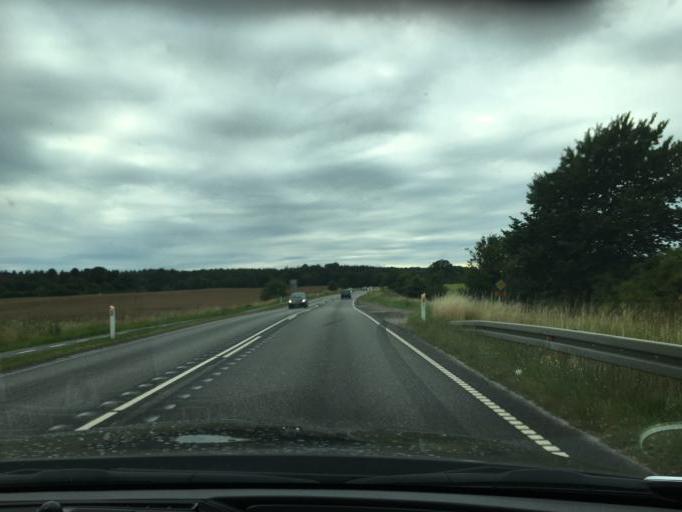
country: DK
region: Capital Region
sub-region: Horsholm Kommune
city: Horsholm
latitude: 55.8775
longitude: 12.4748
